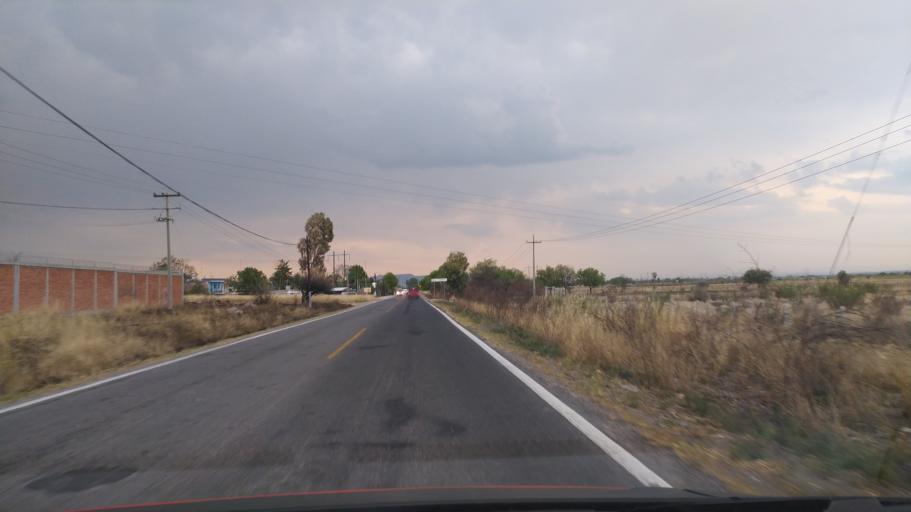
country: MX
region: Guanajuato
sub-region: San Francisco del Rincon
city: San Ignacio de Hidalgo
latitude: 20.8256
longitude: -101.9013
